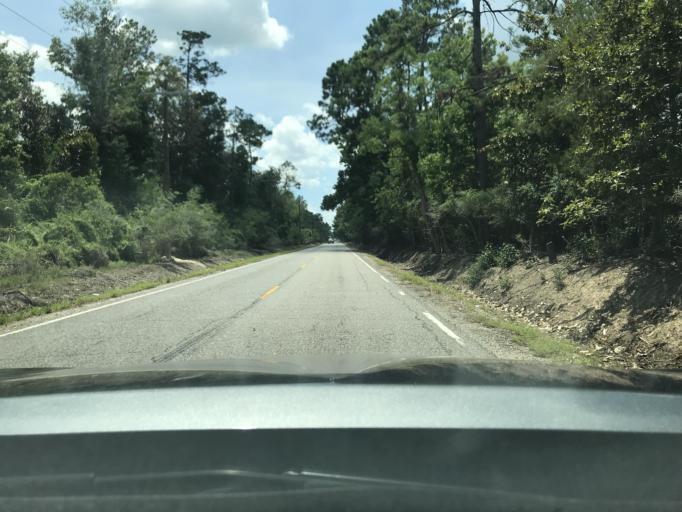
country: US
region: Louisiana
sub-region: Calcasieu Parish
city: Moss Bluff
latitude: 30.3301
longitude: -93.1571
